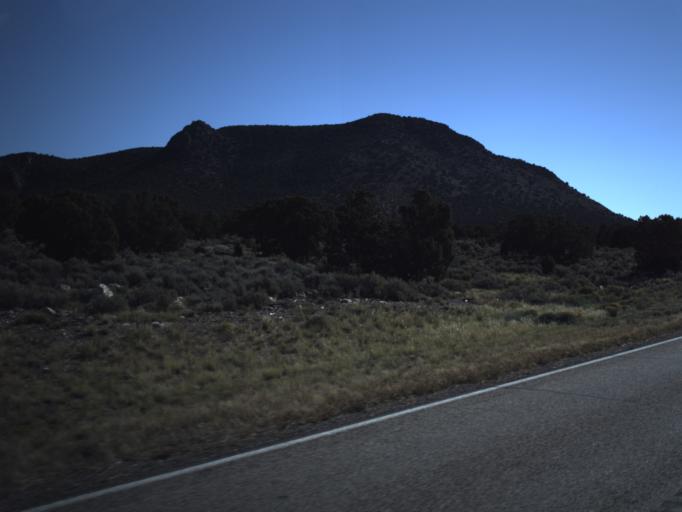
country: US
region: Utah
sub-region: Washington County
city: Enterprise
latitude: 37.6650
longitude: -113.4728
